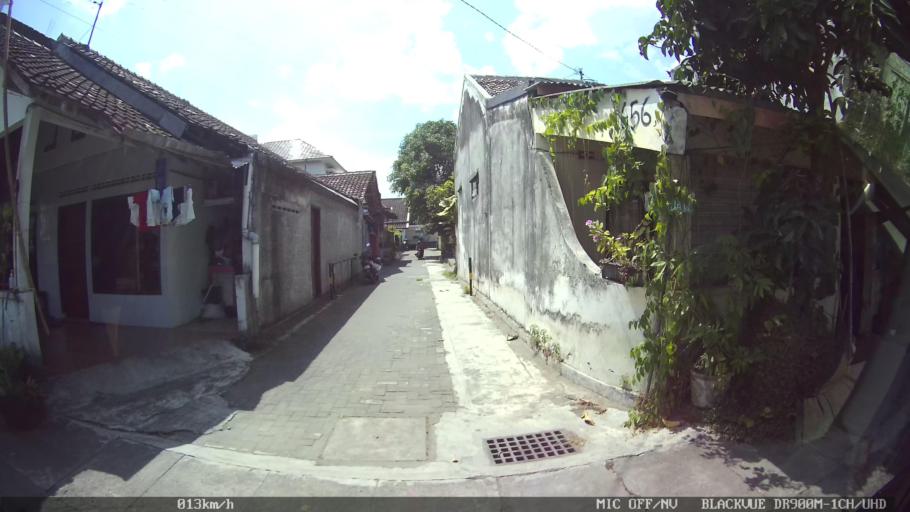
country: ID
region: Daerah Istimewa Yogyakarta
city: Kasihan
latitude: -7.8300
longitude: 110.3778
